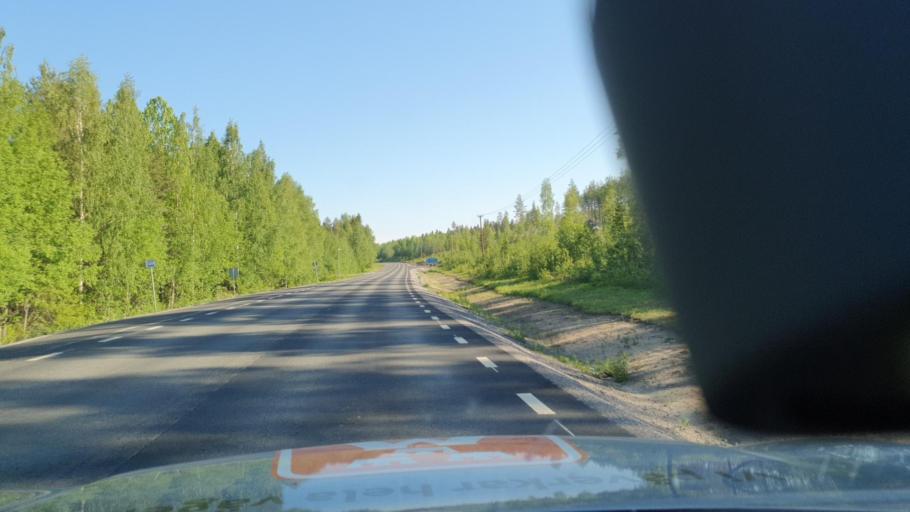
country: SE
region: Norrbotten
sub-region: Alvsbyns Kommun
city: AElvsbyn
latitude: 66.1706
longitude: 20.8788
